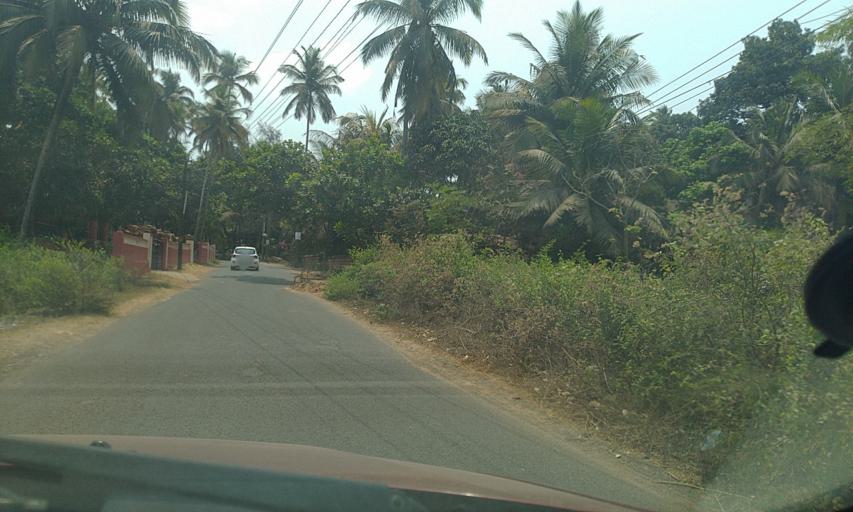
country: IN
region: Goa
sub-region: North Goa
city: Saligao
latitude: 15.5569
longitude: 73.7766
